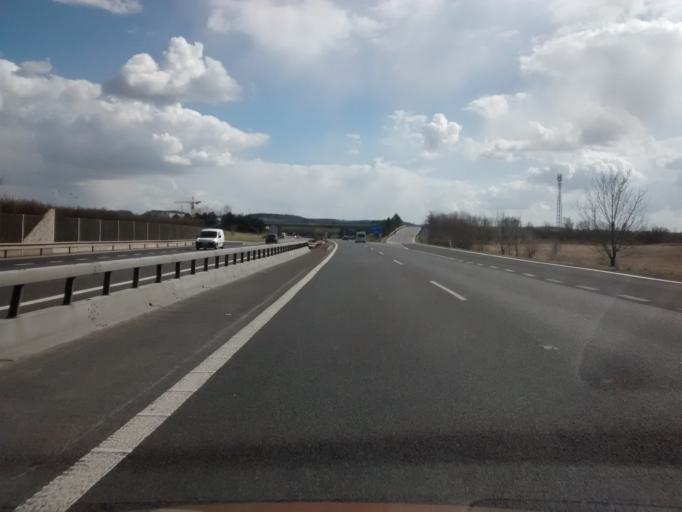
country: CZ
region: Central Bohemia
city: Odolena Voda
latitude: 50.2497
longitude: 14.3730
